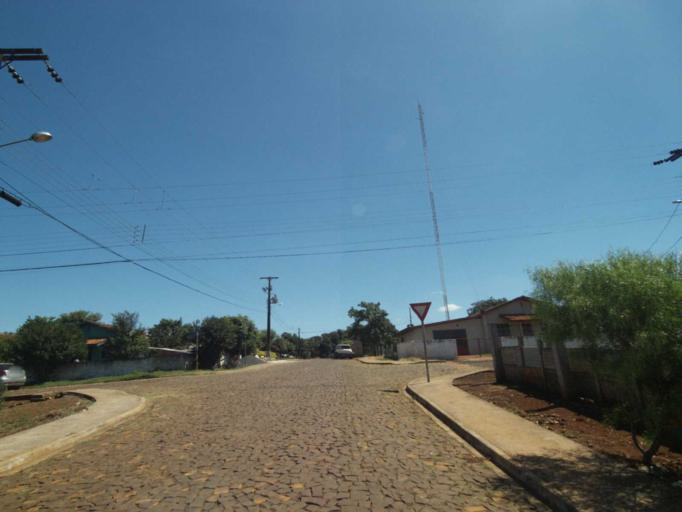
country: BR
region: Parana
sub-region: Laranjeiras Do Sul
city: Laranjeiras do Sul
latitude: -25.3880
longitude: -52.2147
